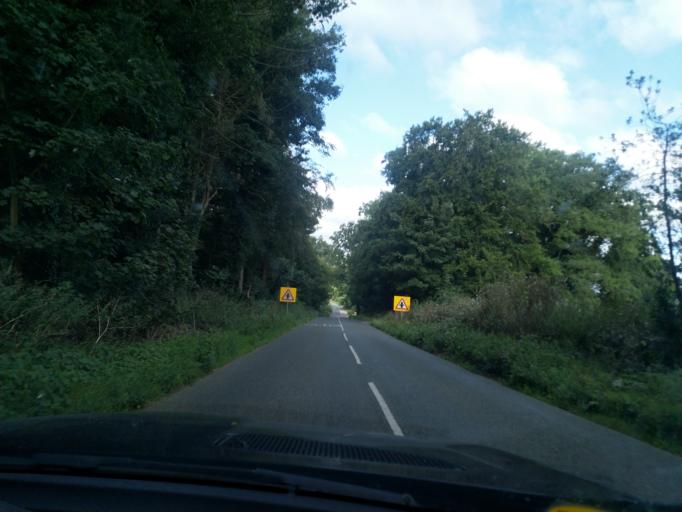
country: GB
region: England
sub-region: Suffolk
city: Thurston
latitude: 52.2463
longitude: 0.8091
